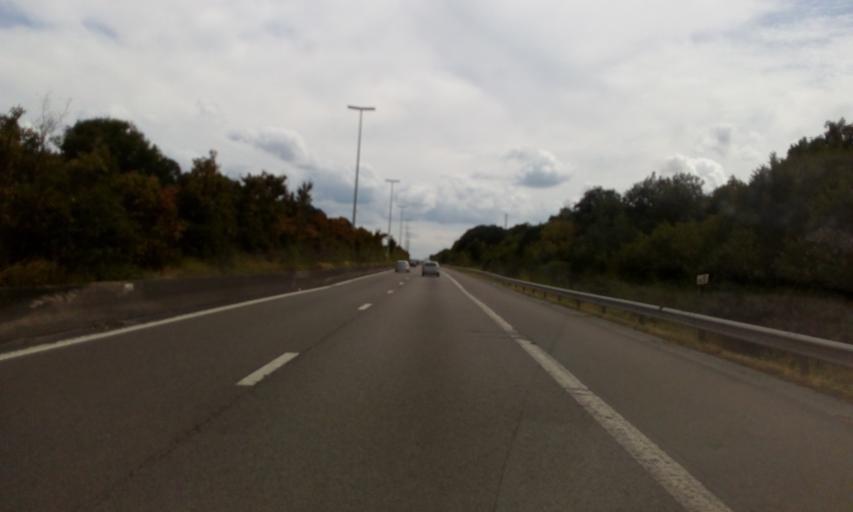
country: BE
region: Wallonia
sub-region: Province du Luxembourg
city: Wellin
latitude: 50.1372
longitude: 5.0831
